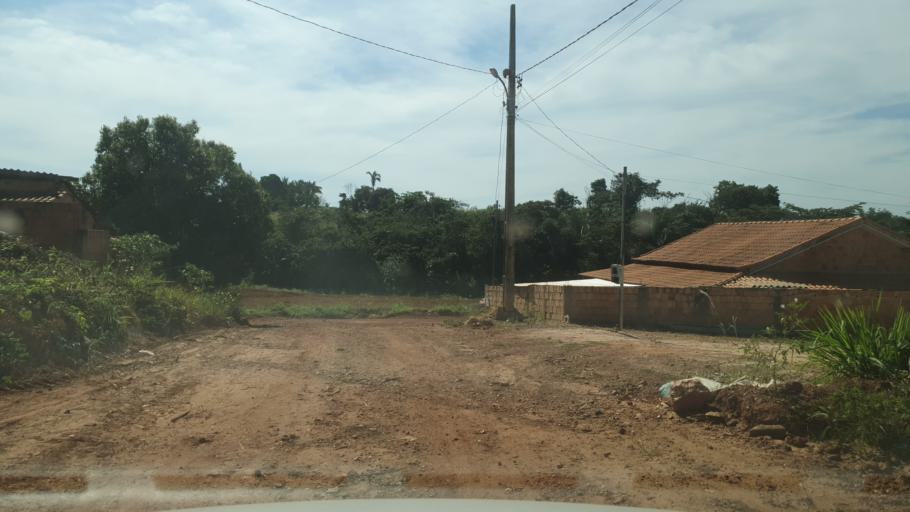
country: BR
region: Mato Grosso
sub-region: Pontes E Lacerda
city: Pontes e Lacerda
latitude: -15.2526
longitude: -59.3133
